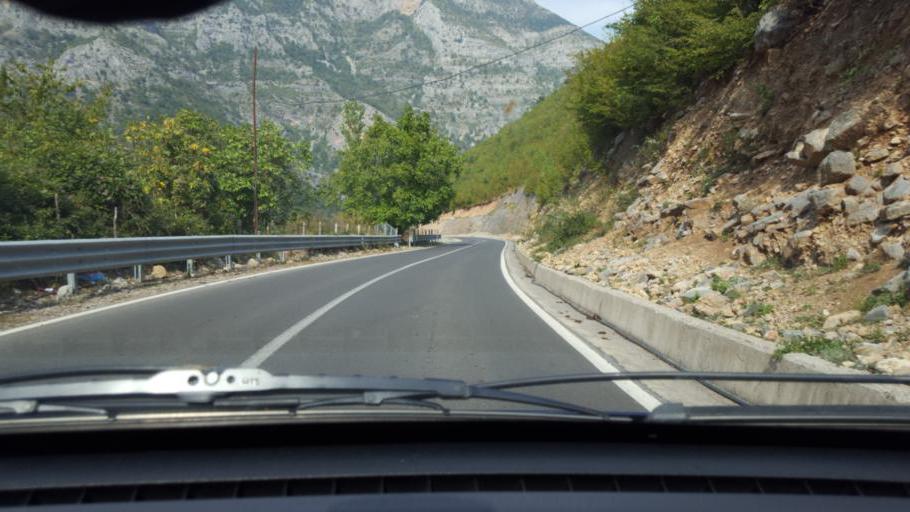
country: AL
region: Shkoder
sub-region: Rrethi i Malesia e Madhe
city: Kastrat
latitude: 42.4180
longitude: 19.5100
